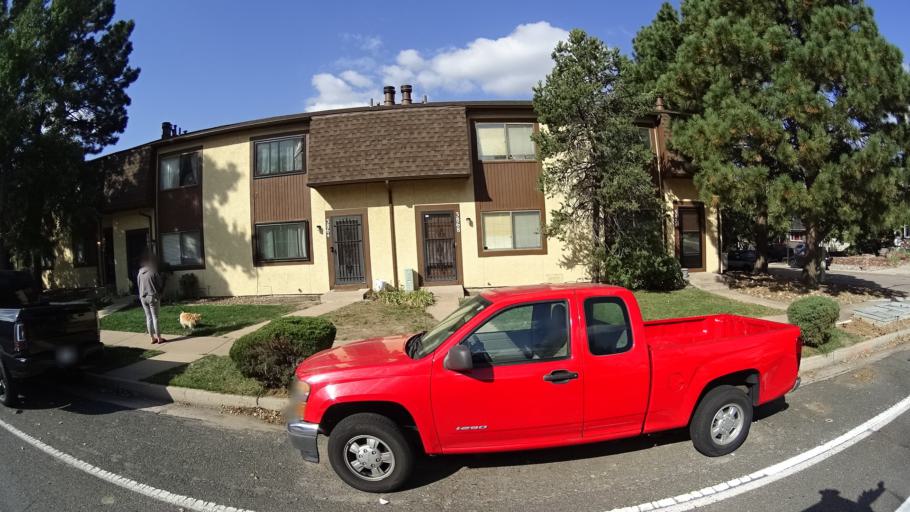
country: US
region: Colorado
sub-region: El Paso County
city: Cimarron Hills
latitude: 38.8880
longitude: -104.7386
